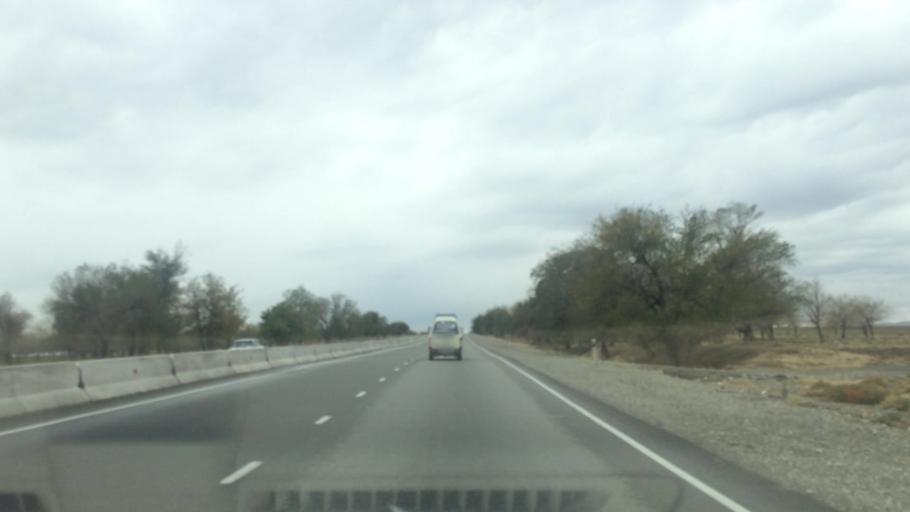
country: UZ
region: Samarqand
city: Bulung'ur
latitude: 39.9345
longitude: 67.5244
